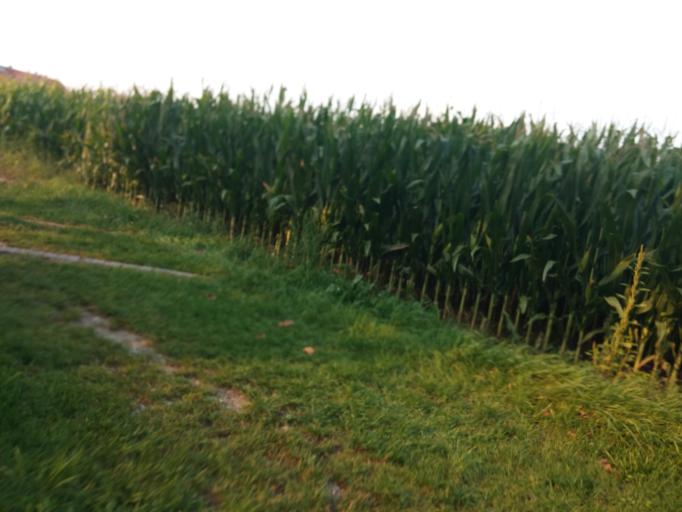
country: DE
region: Bavaria
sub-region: Upper Bavaria
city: Kirchheim bei Muenchen
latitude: 48.1636
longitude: 11.7663
